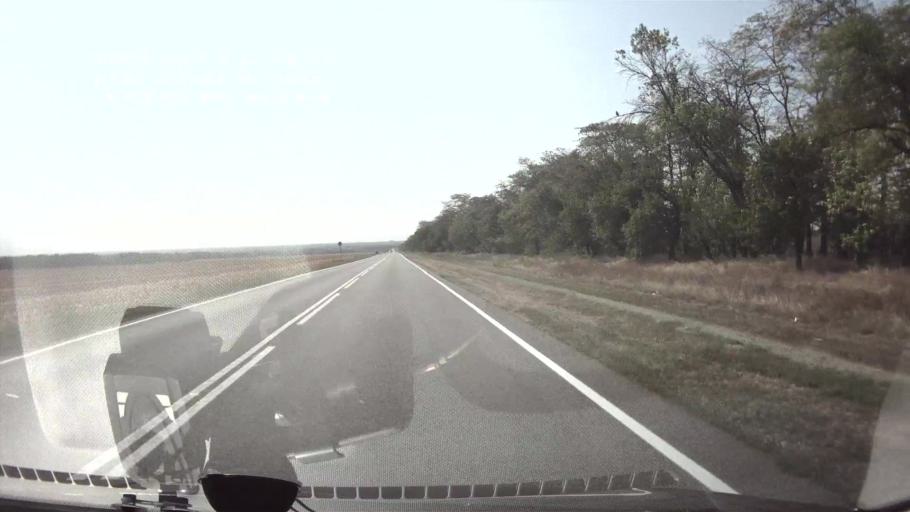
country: RU
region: Krasnodarskiy
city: Dmitriyevskaya
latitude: 45.7730
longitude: 40.7195
